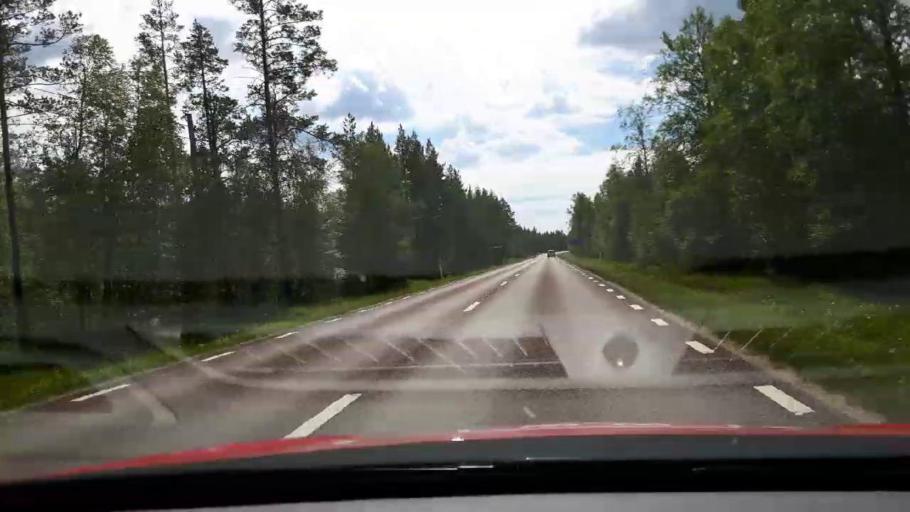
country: SE
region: Jaemtland
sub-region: Harjedalens Kommun
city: Sveg
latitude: 62.1335
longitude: 14.9707
